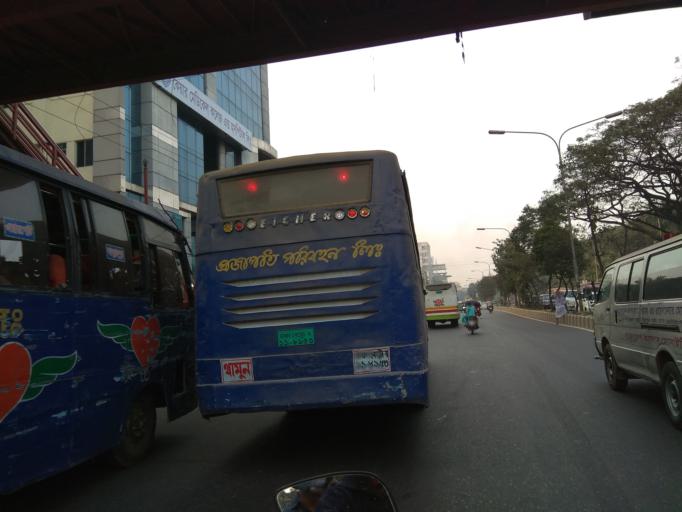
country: BD
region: Dhaka
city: Azimpur
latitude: 23.7688
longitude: 90.3690
